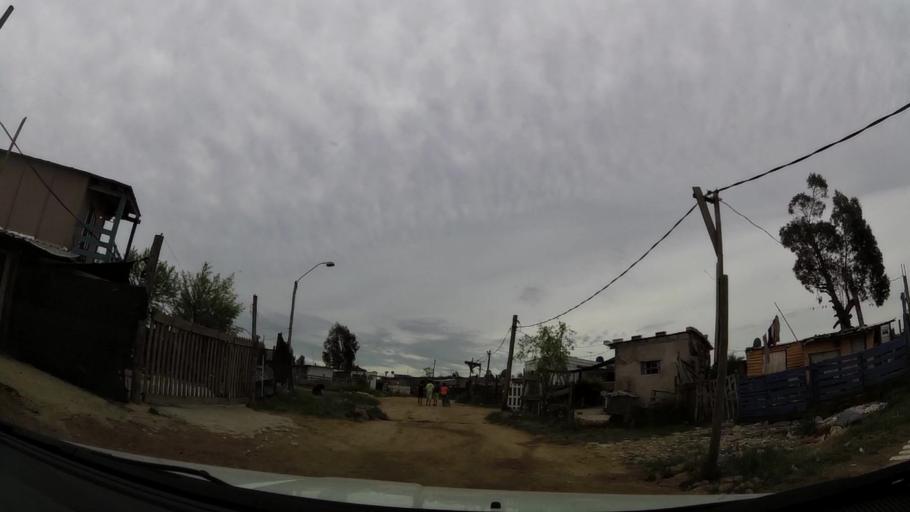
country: UY
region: Maldonado
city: Maldonado
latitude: -34.8867
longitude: -54.9569
